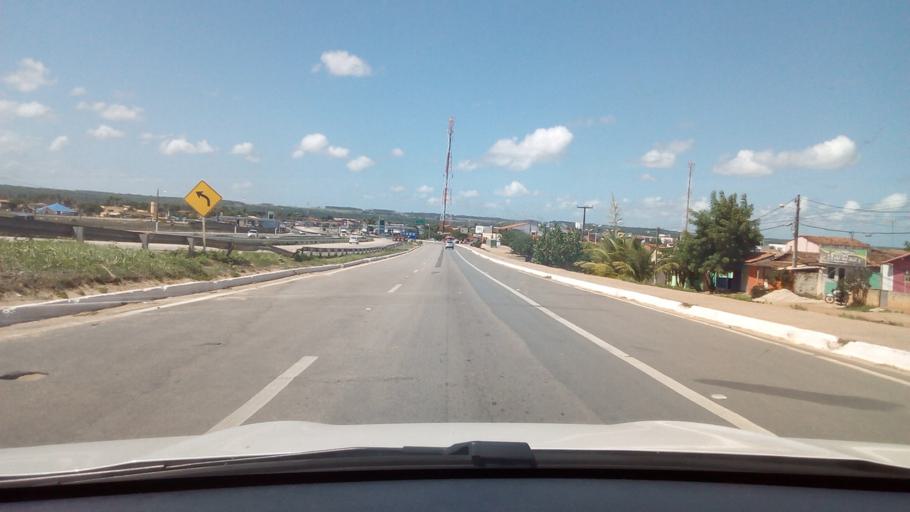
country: BR
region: Rio Grande do Norte
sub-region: Goianinha
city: Goianinha
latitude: -6.2748
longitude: -35.2070
